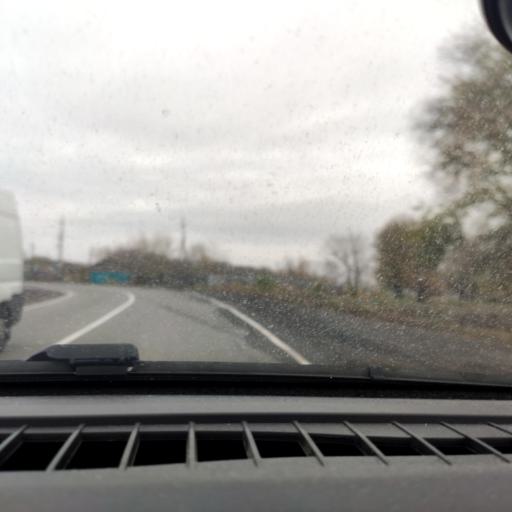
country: RU
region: Voronezj
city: Ostrogozhsk
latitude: 50.7769
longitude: 38.9035
